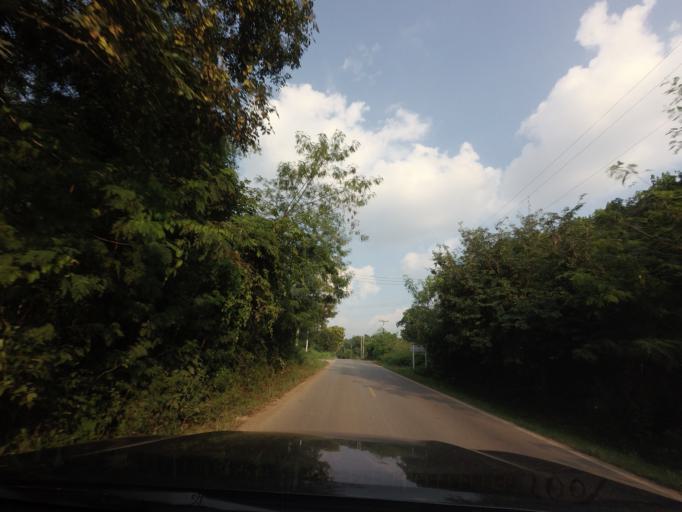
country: TH
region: Nan
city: Nan
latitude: 18.7741
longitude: 100.7411
